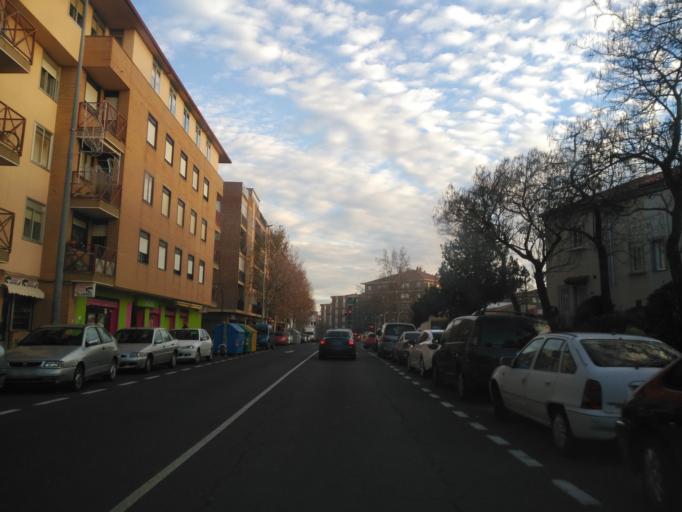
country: ES
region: Castille and Leon
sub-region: Provincia de Salamanca
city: Salamanca
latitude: 40.9756
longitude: -5.6741
